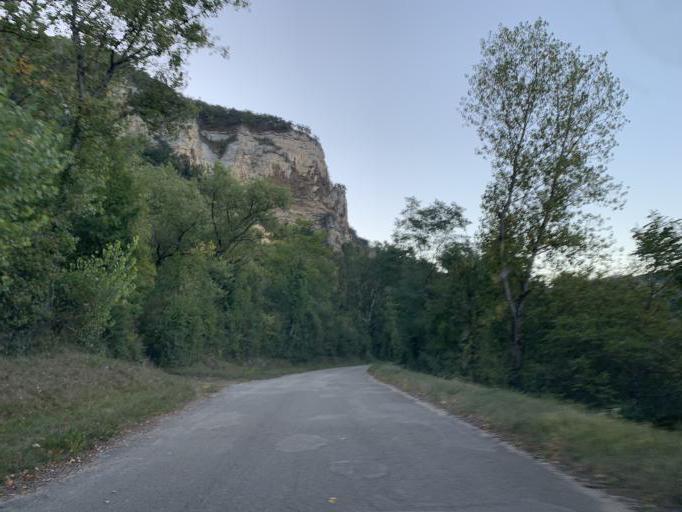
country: FR
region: Rhone-Alpes
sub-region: Departement de l'Ain
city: Vaux-en-Bugey
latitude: 45.9333
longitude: 5.3837
